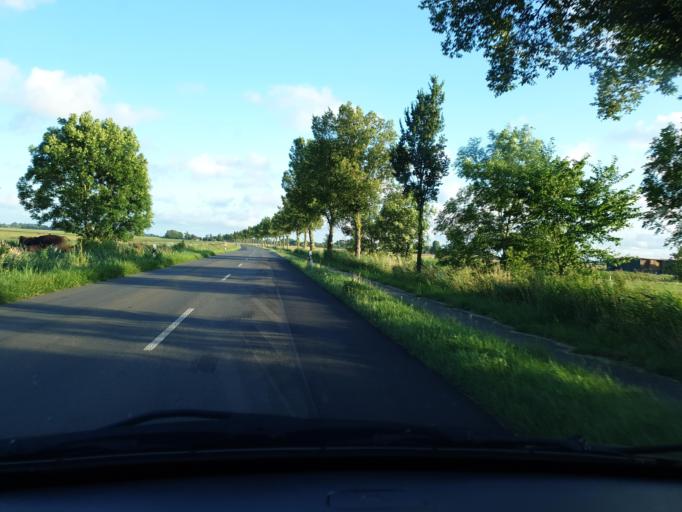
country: DE
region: Schleswig-Holstein
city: Epenwohrden
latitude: 54.1306
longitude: 9.0167
